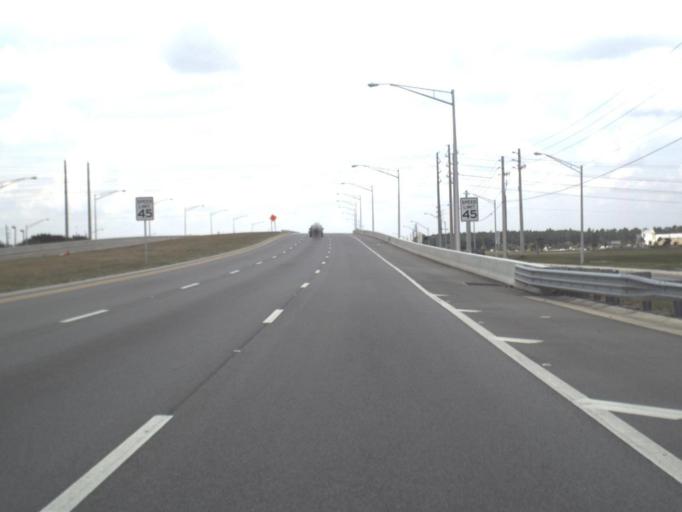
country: US
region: Florida
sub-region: Duval County
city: Atlantic Beach
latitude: 30.3191
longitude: -81.4858
